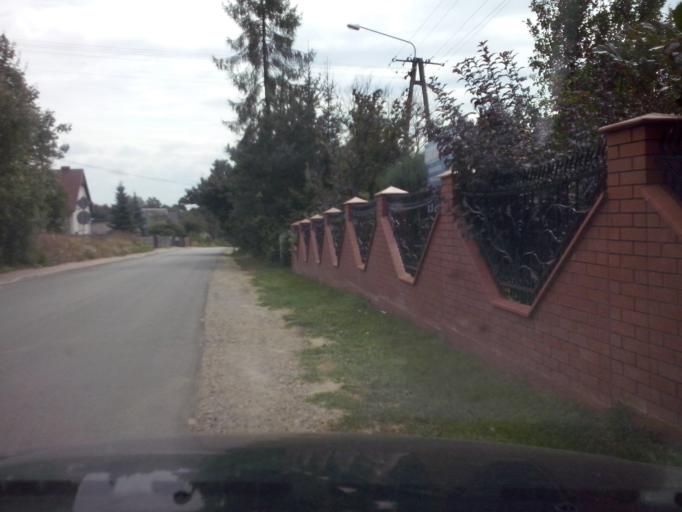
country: PL
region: Swietokrzyskie
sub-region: Powiat kielecki
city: Lagow
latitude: 50.7250
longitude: 21.1065
